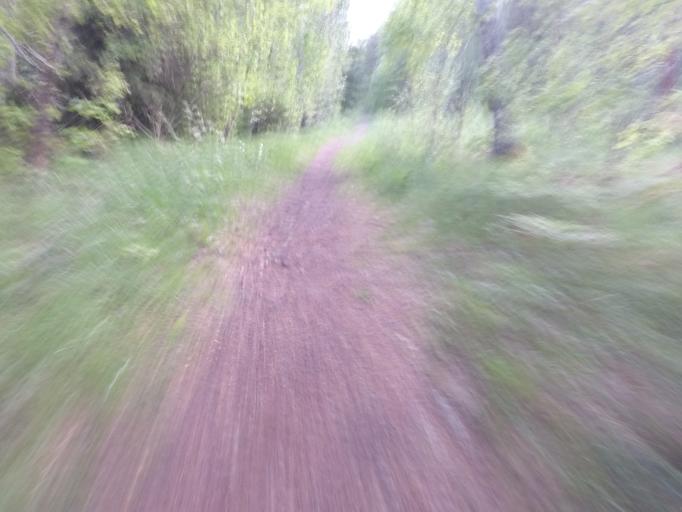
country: SE
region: Soedermanland
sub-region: Eskilstuna Kommun
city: Hallbybrunn
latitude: 59.3928
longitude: 16.4021
